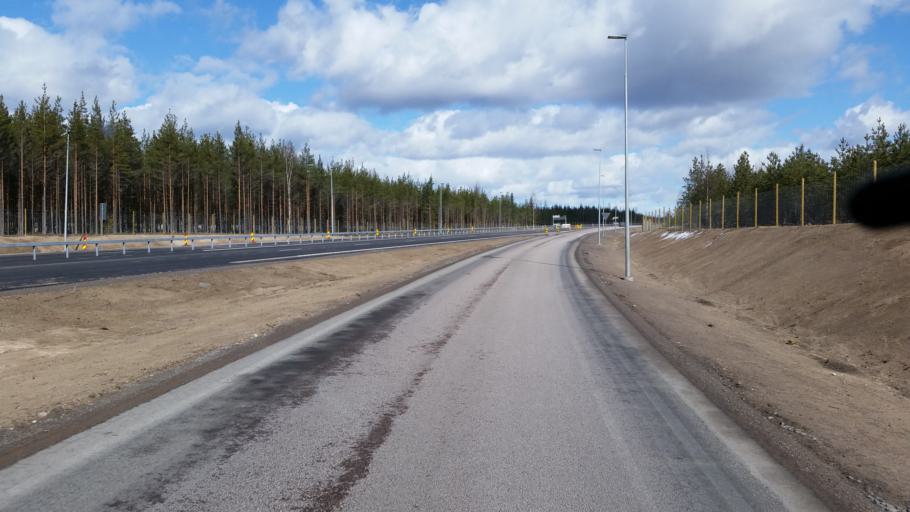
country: FI
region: South Karelia
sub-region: Lappeenranta
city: Lemi
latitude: 60.9771
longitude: 27.8747
